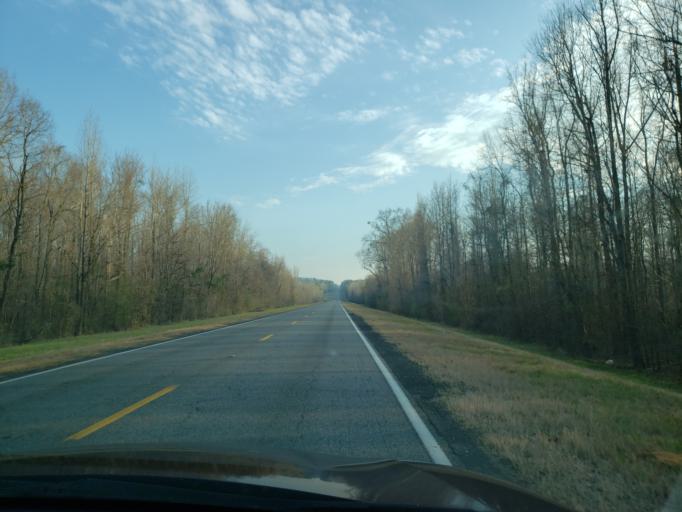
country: US
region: Alabama
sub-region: Hale County
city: Greensboro
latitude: 32.7674
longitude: -87.5854
